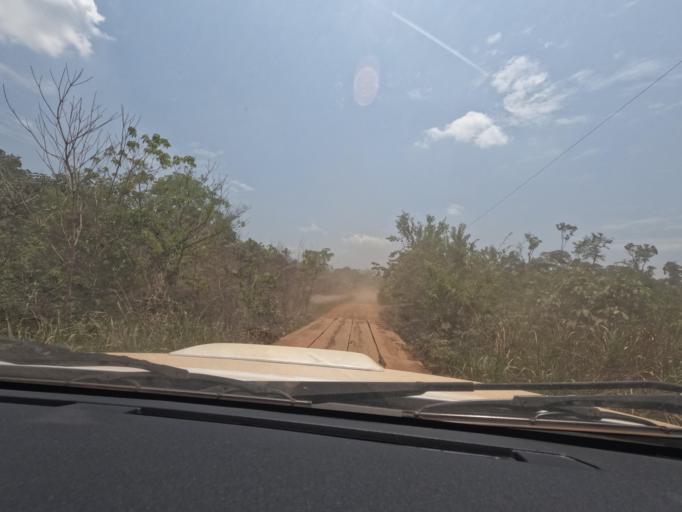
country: BR
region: Rondonia
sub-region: Porto Velho
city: Porto Velho
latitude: -8.6559
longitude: -64.1664
